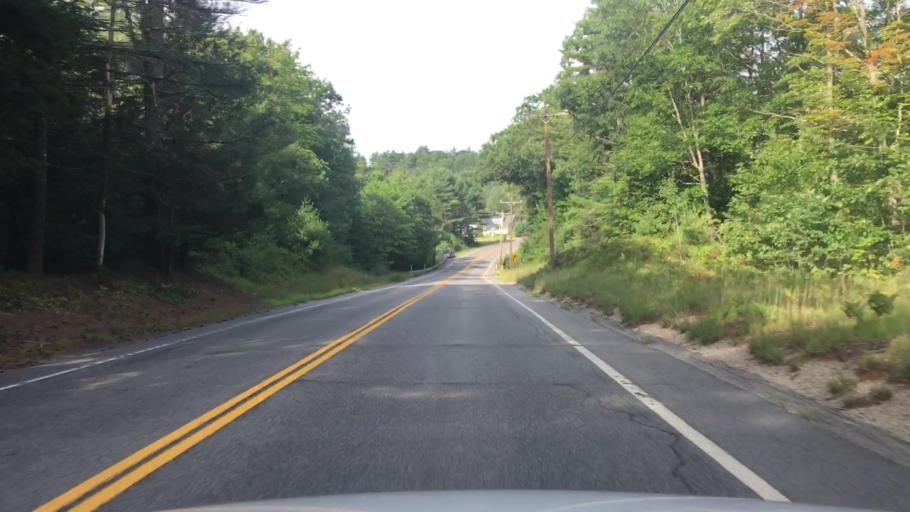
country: US
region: Maine
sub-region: York County
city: Cornish
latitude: 43.8038
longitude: -70.8508
